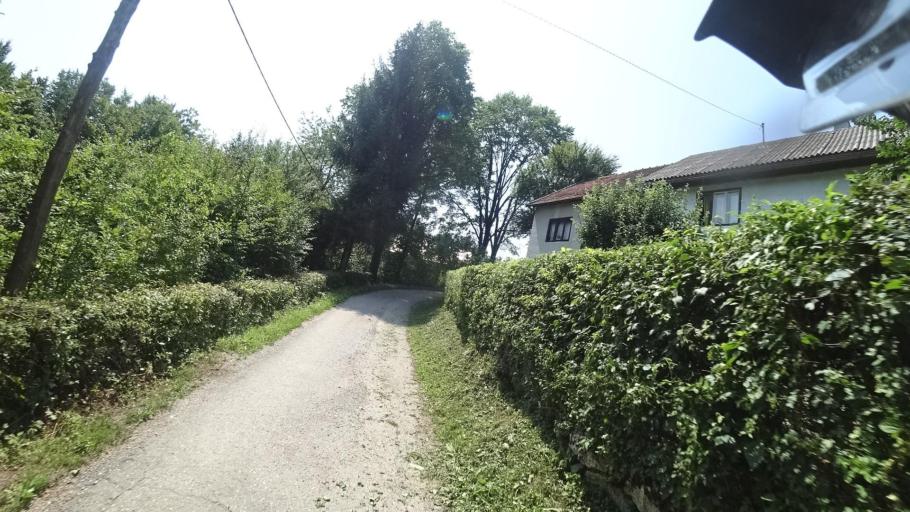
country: HR
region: Karlovacka
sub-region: Grad Ogulin
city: Ogulin
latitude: 45.3114
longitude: 15.1760
